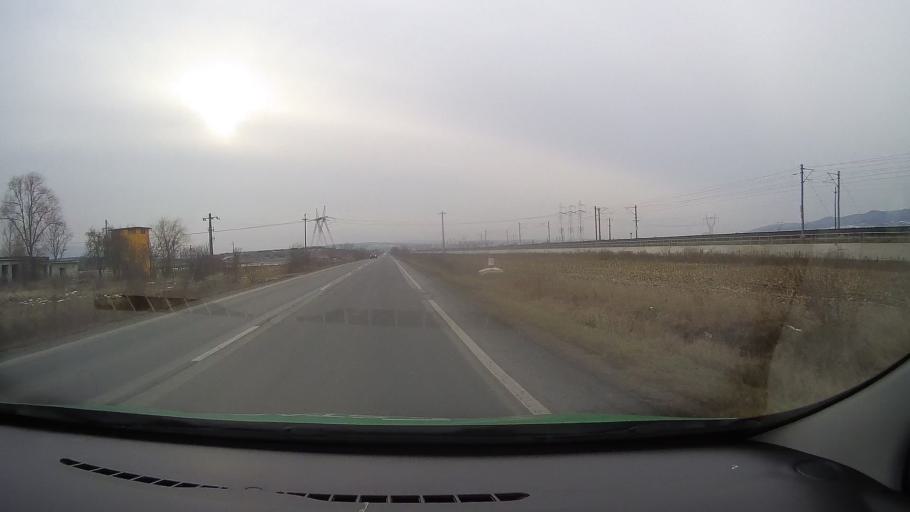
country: RO
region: Hunedoara
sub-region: Comuna Geoagiu
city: Geoagiu
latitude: 45.8764
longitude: 23.2384
